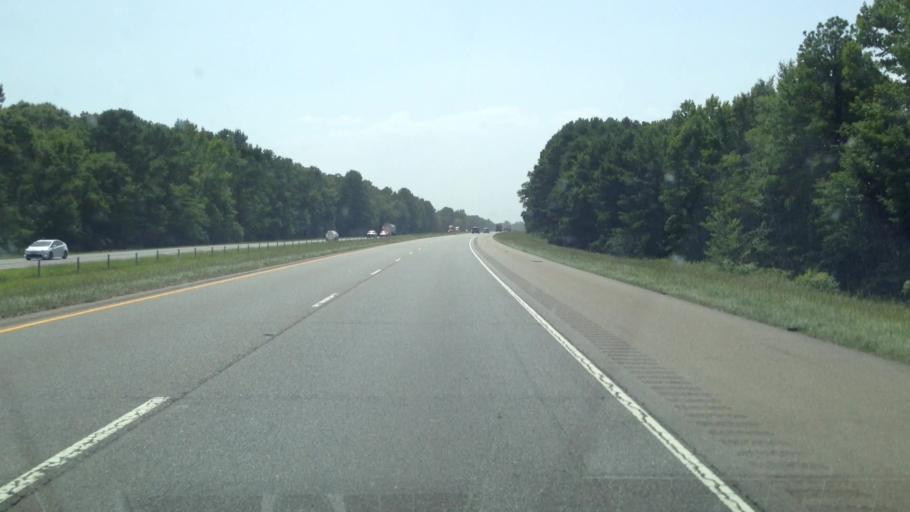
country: US
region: Louisiana
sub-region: Bossier Parish
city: Haughton
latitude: 32.5774
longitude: -93.4489
